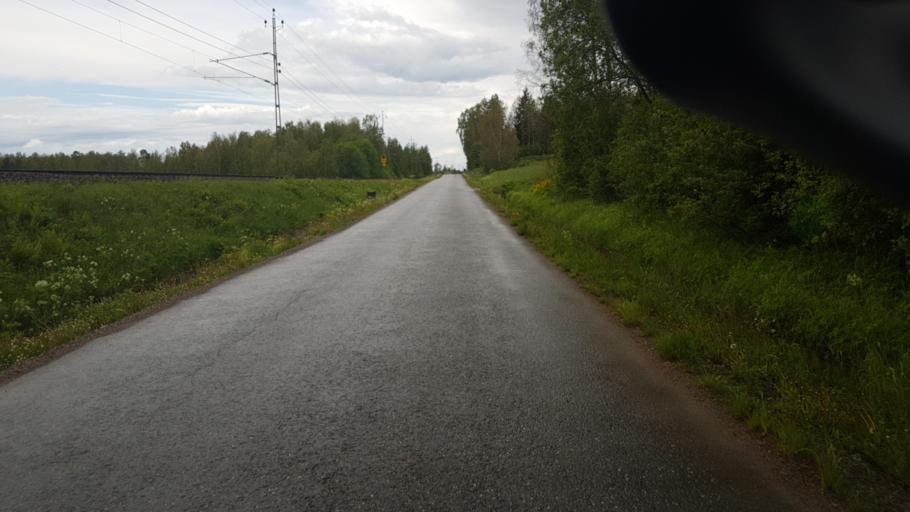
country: SE
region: Vaermland
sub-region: Eda Kommun
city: Amotfors
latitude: 59.7970
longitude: 12.3694
